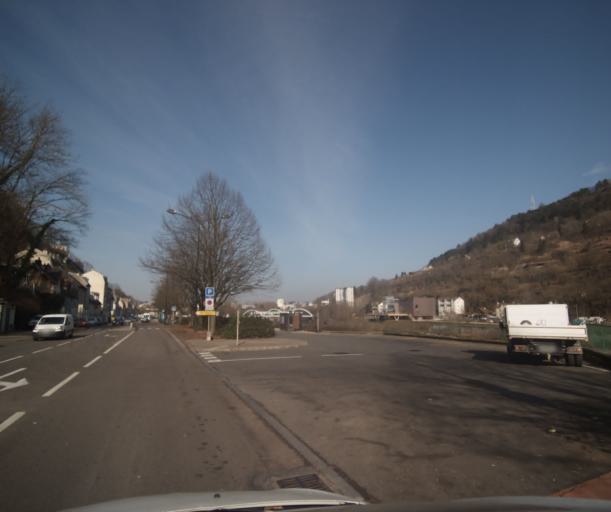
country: FR
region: Franche-Comte
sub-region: Departement du Doubs
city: Besancon
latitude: 47.2299
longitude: 6.0371
